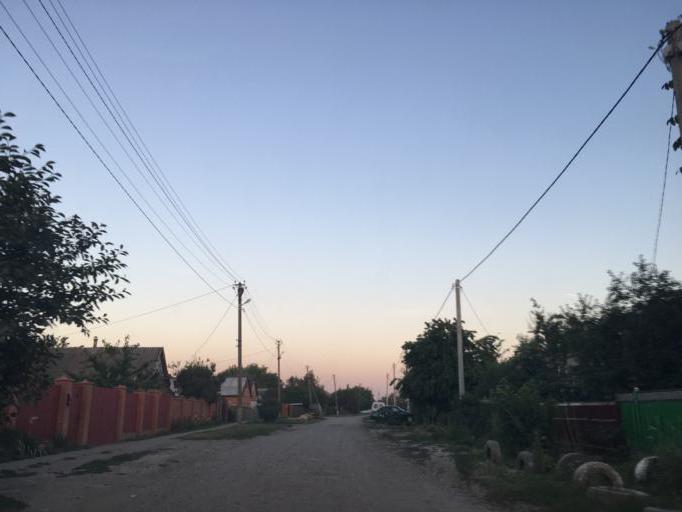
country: RU
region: Krasnodarskiy
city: Kushchevskaya
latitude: 46.5637
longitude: 39.6413
